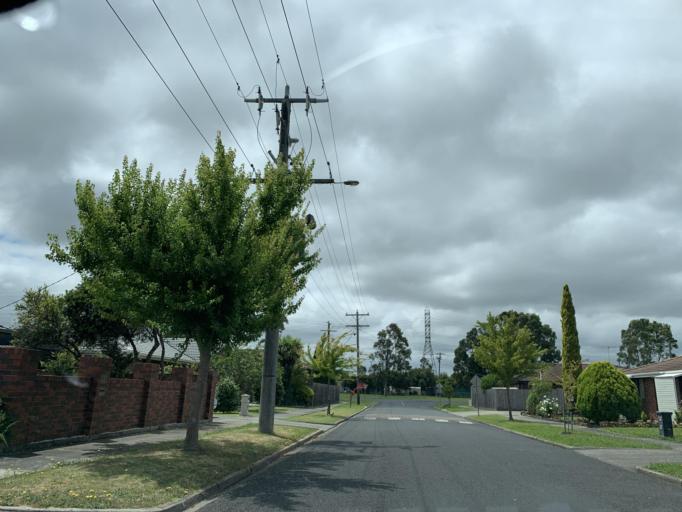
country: AU
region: Victoria
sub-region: Latrobe
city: Moe
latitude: -38.1629
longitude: 146.2656
